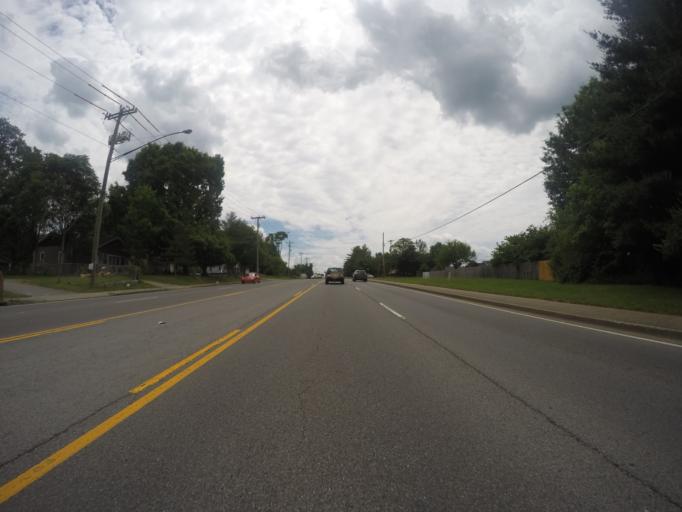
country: US
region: Tennessee
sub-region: Davidson County
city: Lakewood
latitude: 36.2214
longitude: -86.6251
